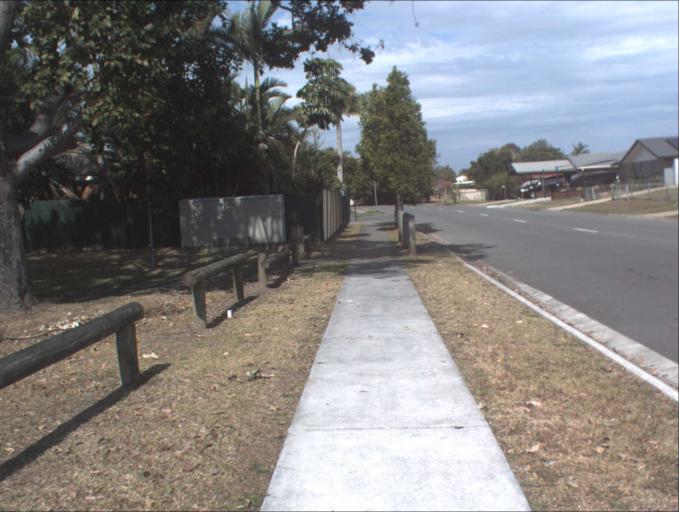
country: AU
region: Queensland
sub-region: Logan
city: Beenleigh
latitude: -27.6816
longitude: 153.1771
